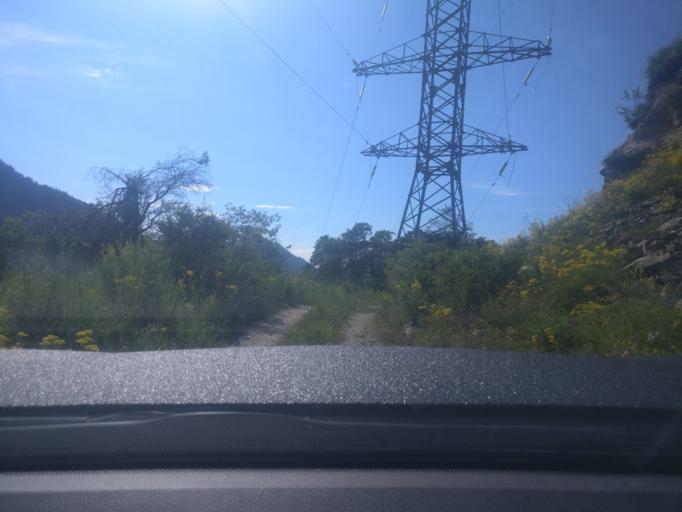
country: KZ
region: Almaty Qalasy
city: Almaty
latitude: 43.0991
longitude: 76.9531
